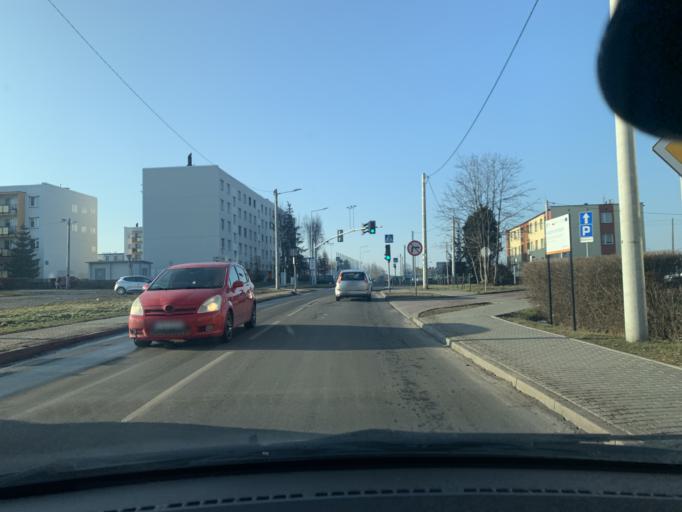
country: PL
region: Silesian Voivodeship
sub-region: Powiat tarnogorski
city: Radzionkow
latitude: 50.4043
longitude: 18.9029
